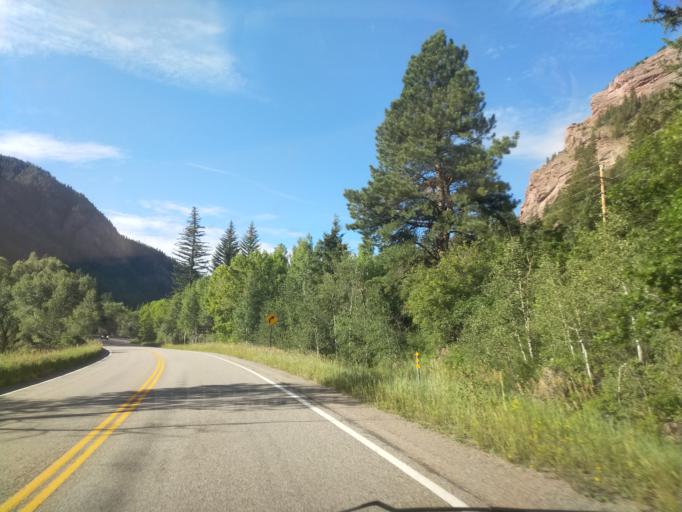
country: US
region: Colorado
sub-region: Garfield County
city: Carbondale
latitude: 39.2053
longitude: -107.2317
